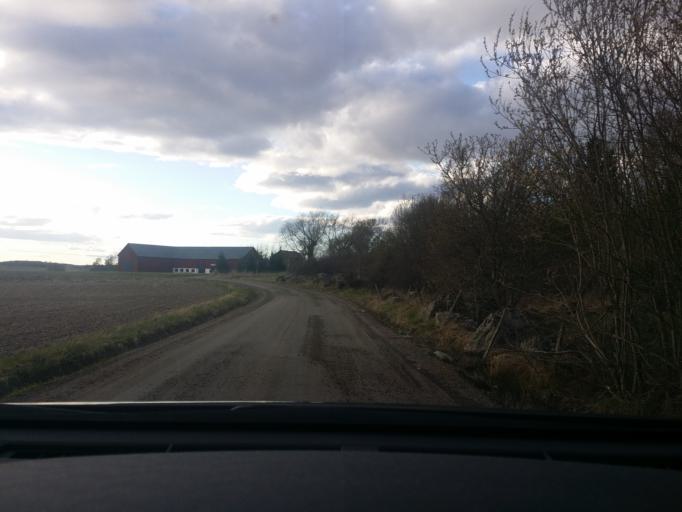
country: SE
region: Vaestmanland
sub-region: Vasteras
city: Vasteras
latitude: 59.5512
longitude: 16.4586
